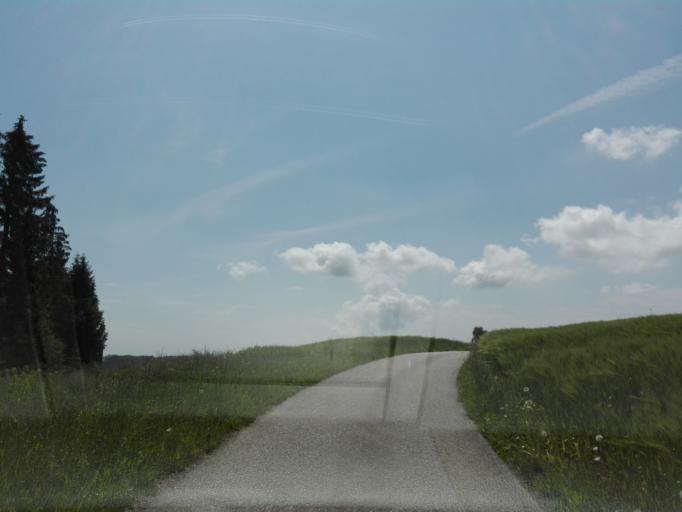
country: AT
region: Upper Austria
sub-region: Politischer Bezirk Rohrbach
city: Atzesberg
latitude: 48.4324
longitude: 13.9110
